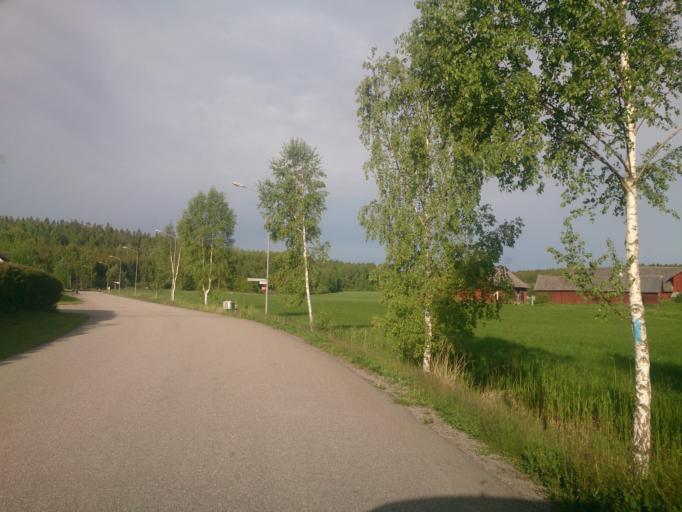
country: SE
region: OEstergoetland
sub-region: Atvidabergs Kommun
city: Atvidaberg
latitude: 58.3330
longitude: 16.0192
